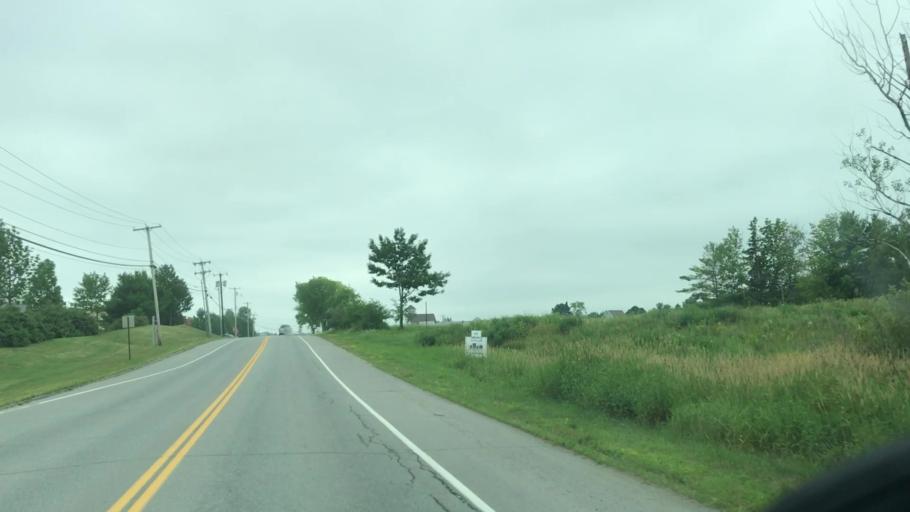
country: US
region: Maine
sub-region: Penobscot County
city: Veazie
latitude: 44.8445
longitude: -68.7413
